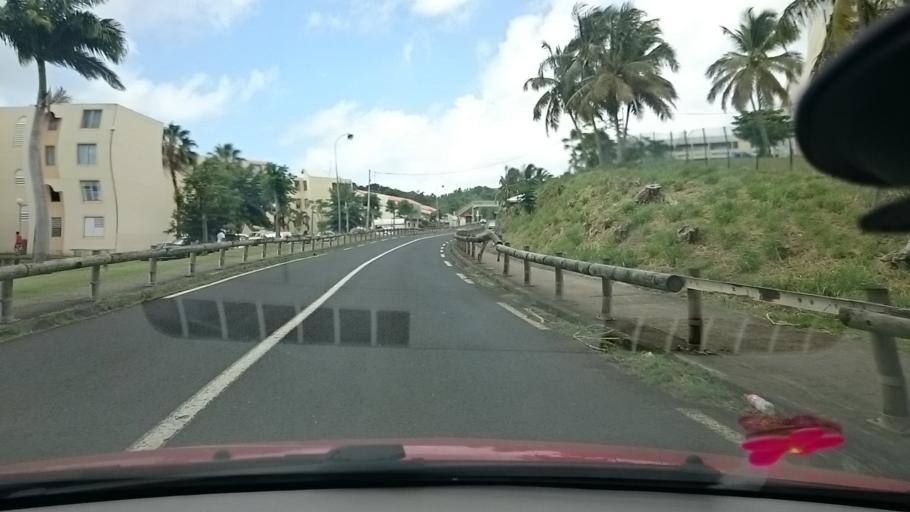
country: MQ
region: Martinique
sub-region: Martinique
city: La Trinite
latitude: 14.7456
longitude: -60.9466
